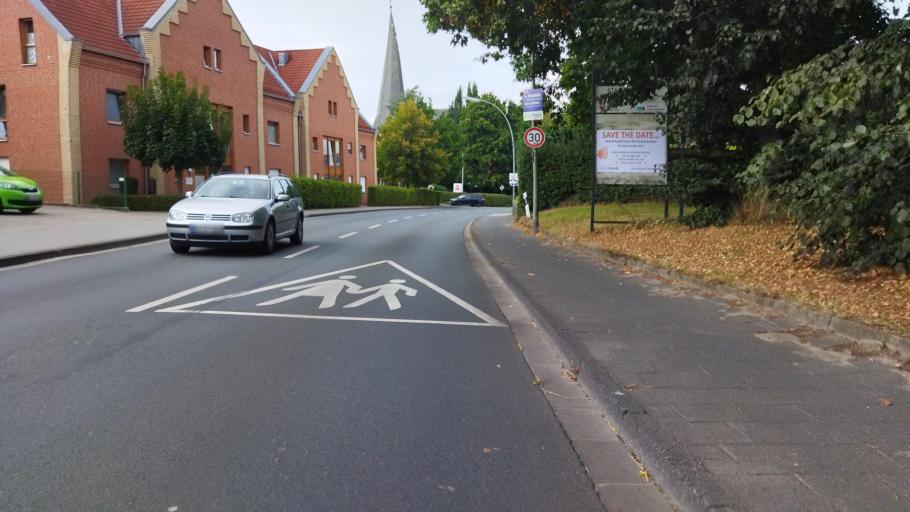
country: DE
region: North Rhine-Westphalia
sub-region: Regierungsbezirk Munster
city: Telgte
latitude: 52.0216
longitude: 7.7807
